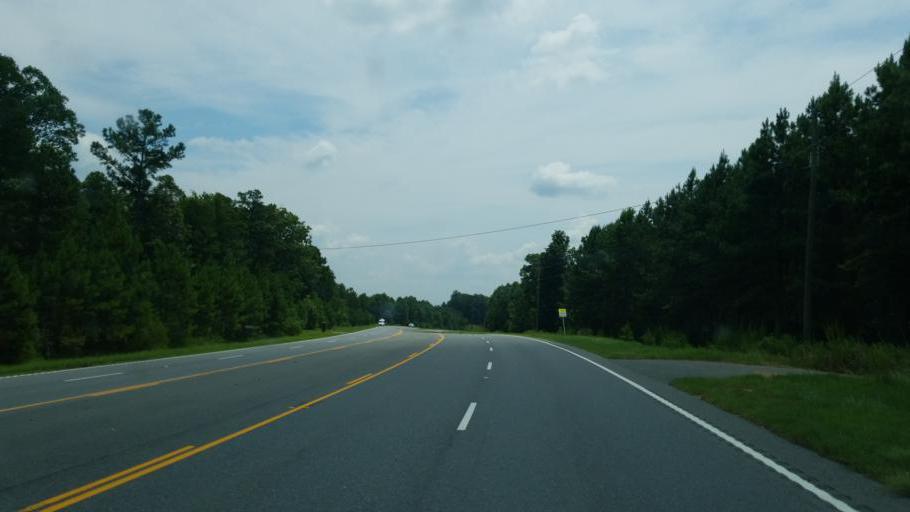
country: US
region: South Carolina
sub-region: Cherokee County
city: Blacksburg
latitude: 35.0663
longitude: -81.4027
